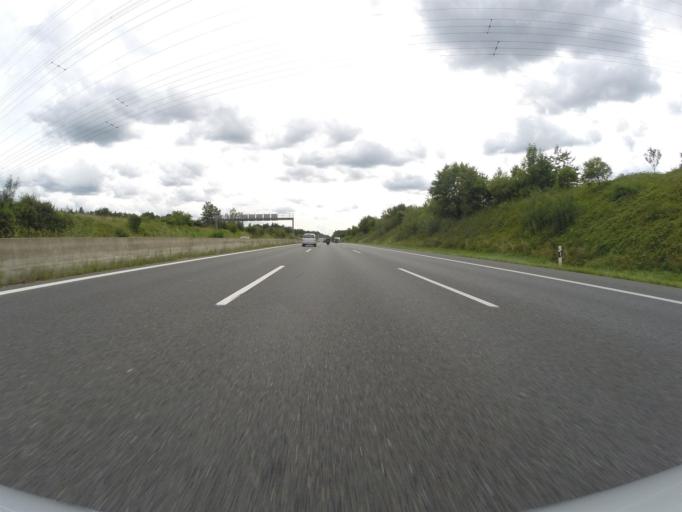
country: DE
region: Bavaria
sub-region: Regierungsbezirk Mittelfranken
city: Lauf an der Pegnitz
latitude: 49.4888
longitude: 11.2752
